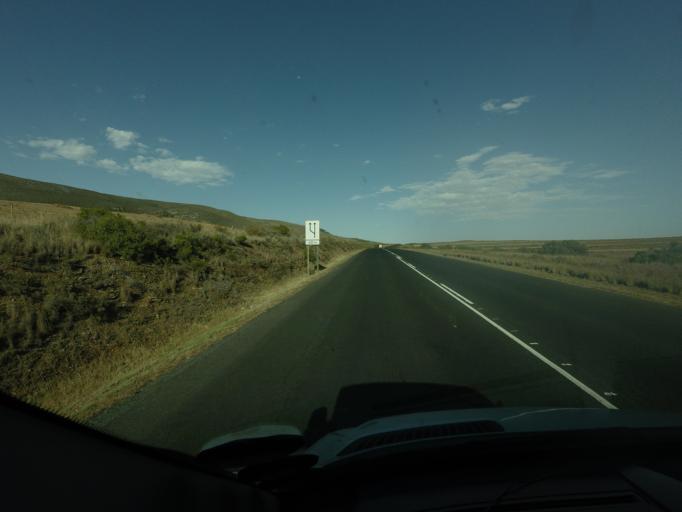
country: ZA
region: Western Cape
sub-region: Overberg District Municipality
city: Swellendam
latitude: -34.0985
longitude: 20.1717
